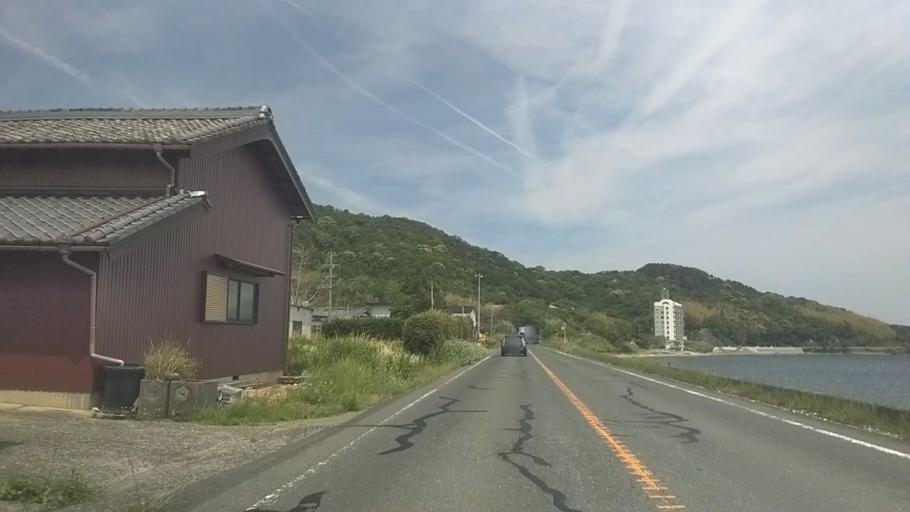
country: JP
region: Shizuoka
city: Kosai-shi
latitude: 34.7678
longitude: 137.5358
